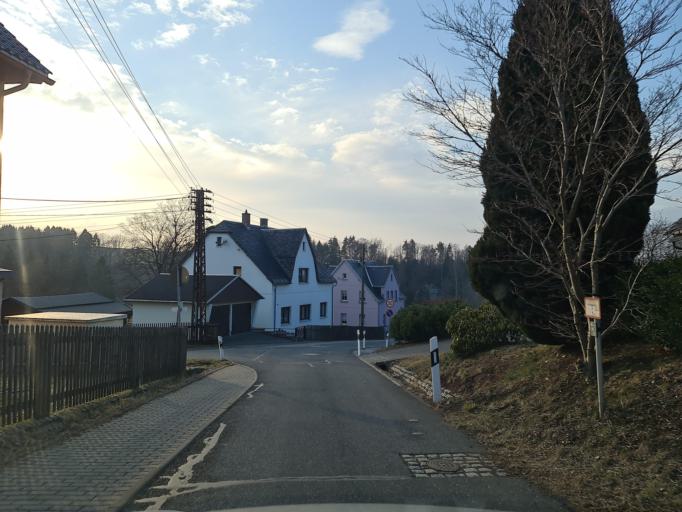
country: DE
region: Saxony
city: Auerbach
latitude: 50.4985
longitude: 12.4379
